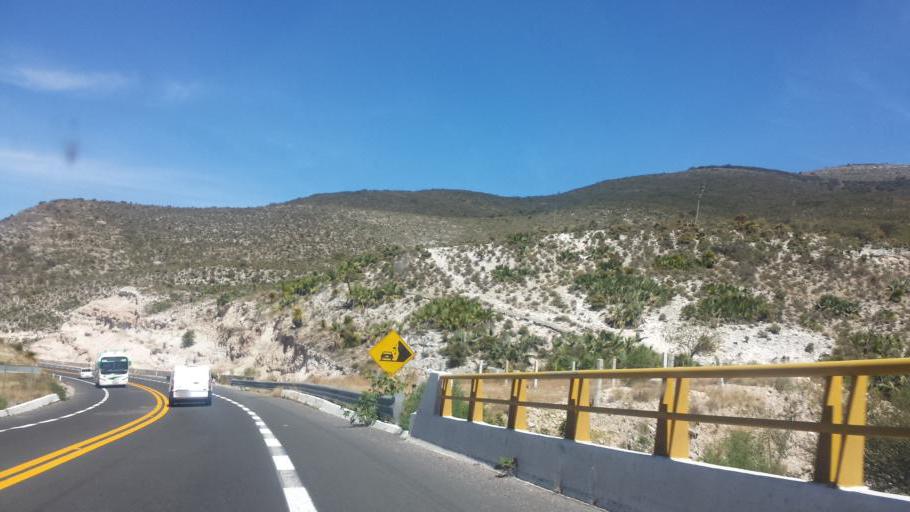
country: MX
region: Oaxaca
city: San Gabriel Casa Blanca
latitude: 17.9833
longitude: -97.3532
